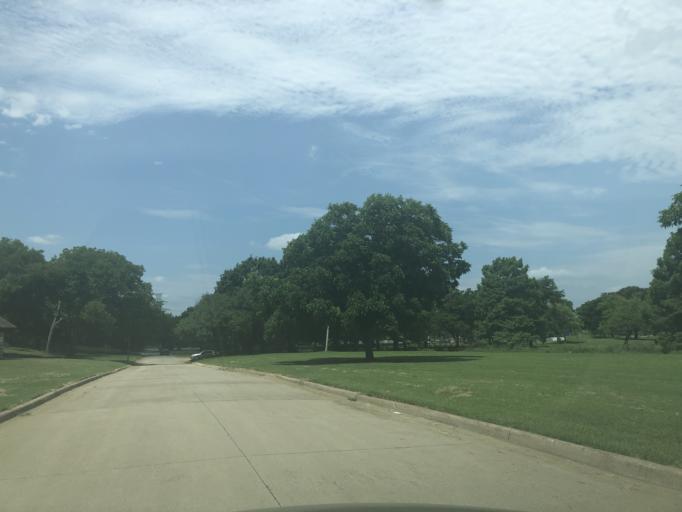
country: US
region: Texas
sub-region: Dallas County
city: Grand Prairie
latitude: 32.7250
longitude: -97.0131
